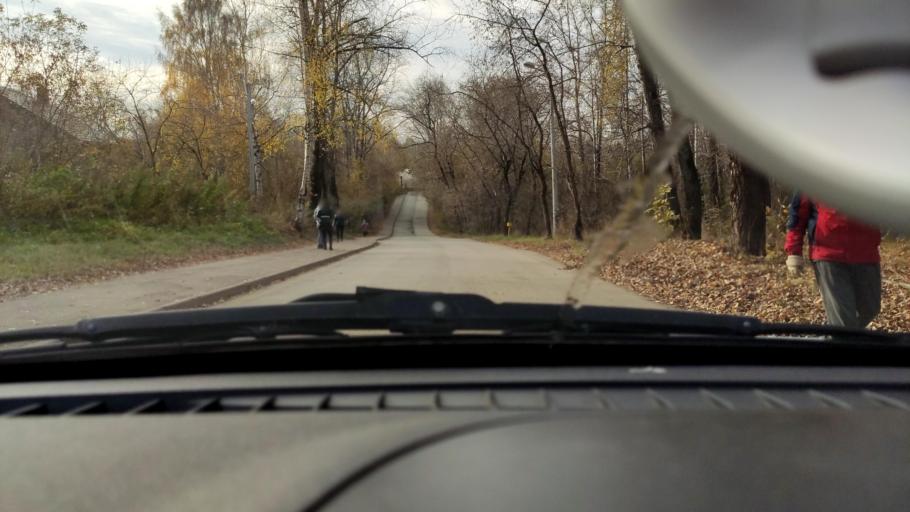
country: RU
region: Perm
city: Polazna
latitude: 58.1247
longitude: 56.3832
